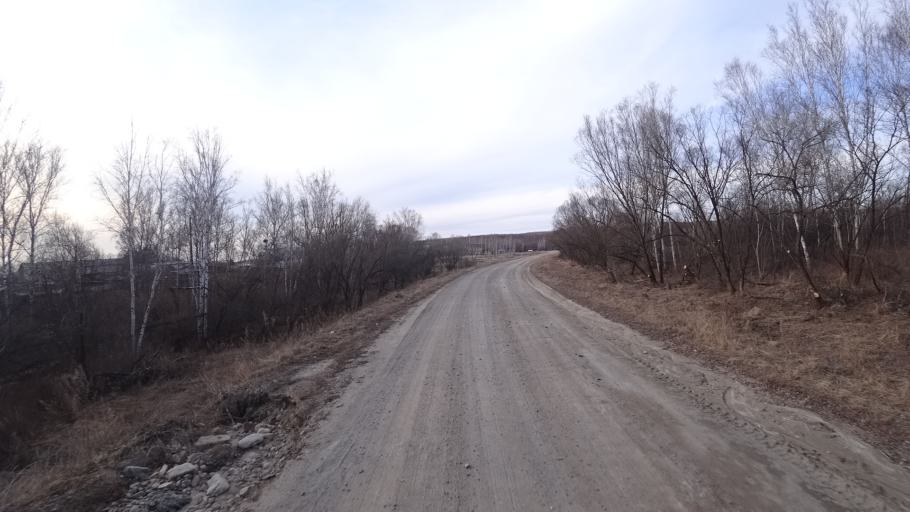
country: RU
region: Amur
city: Bureya
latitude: 50.0171
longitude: 129.7734
